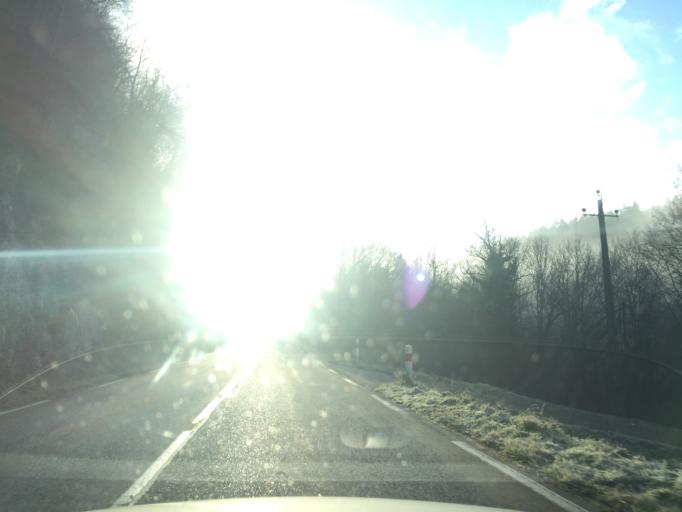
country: FR
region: Rhone-Alpes
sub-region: Departement de la Haute-Savoie
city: Gruffy
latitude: 45.7247
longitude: 6.0956
